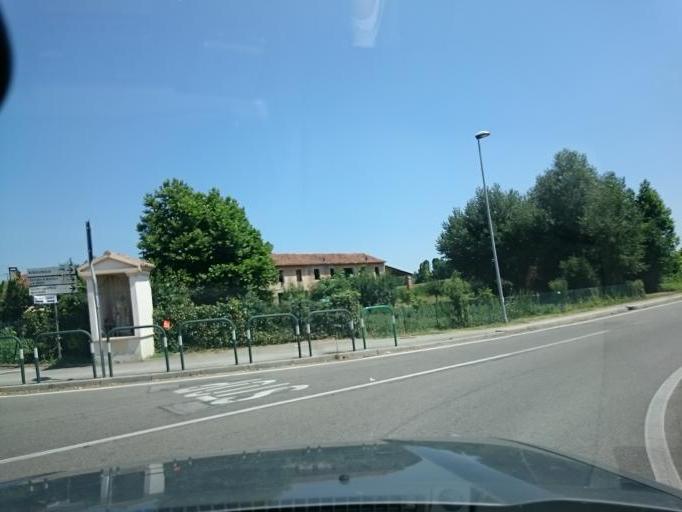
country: IT
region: Veneto
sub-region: Provincia di Padova
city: Caselle
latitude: 45.4083
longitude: 11.8276
